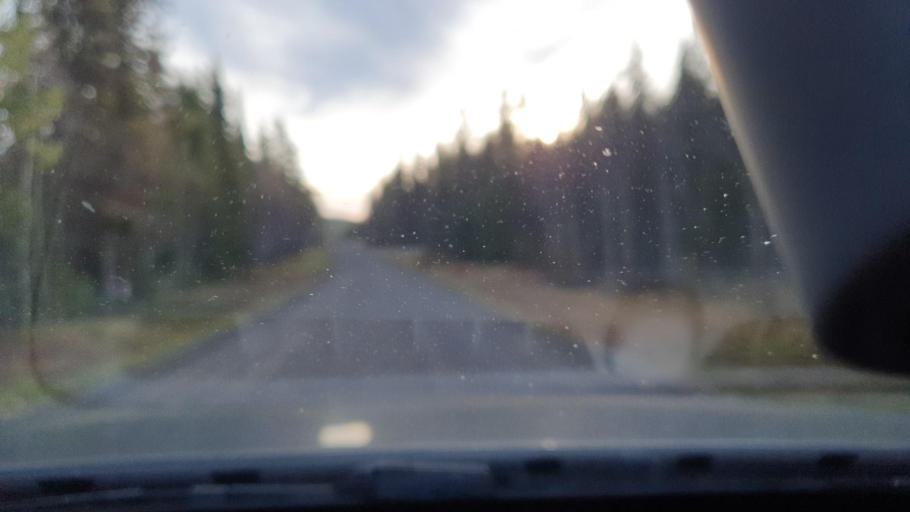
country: SE
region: Jaemtland
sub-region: Stroemsunds Kommun
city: Stroemsund
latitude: 63.5433
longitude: 15.5673
